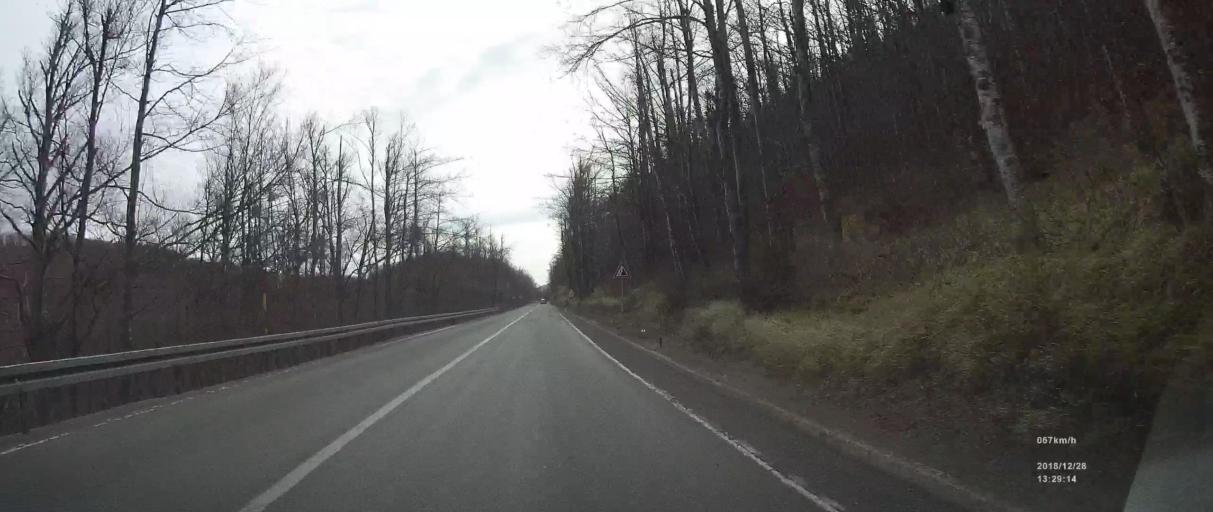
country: HR
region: Primorsko-Goranska
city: Hreljin
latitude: 45.3627
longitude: 14.6267
